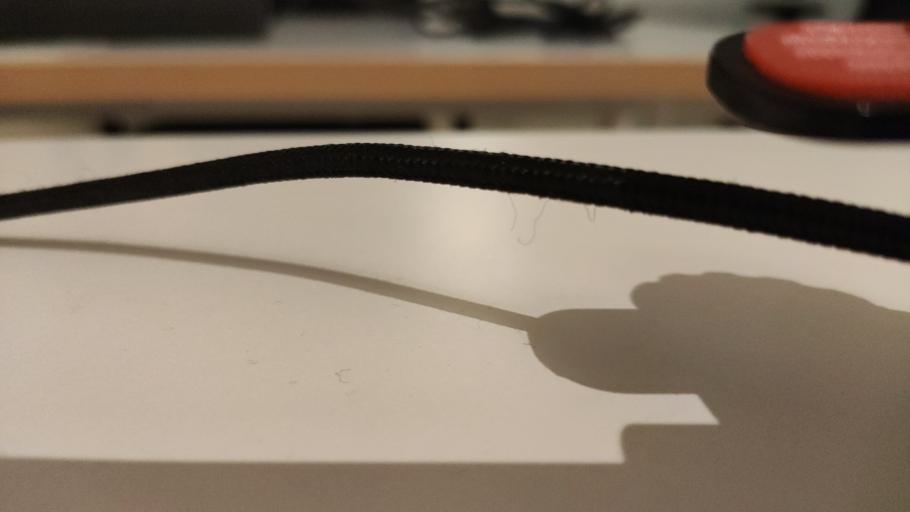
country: RU
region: Moskovskaya
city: Shaburnovo
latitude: 56.4393
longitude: 37.9087
